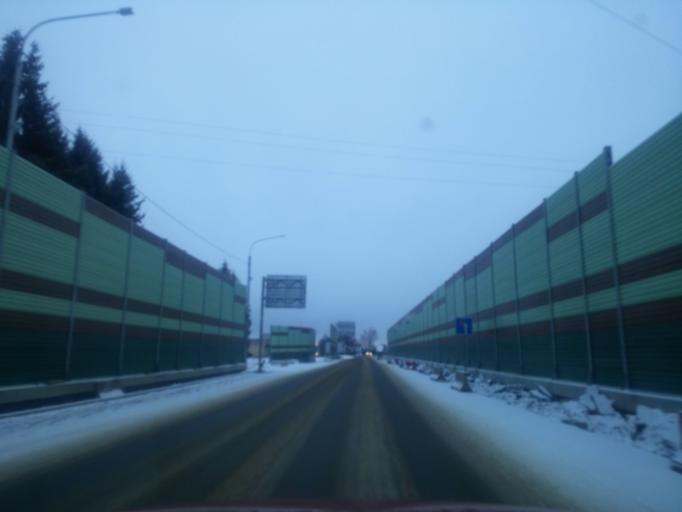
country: RU
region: Tverskaya
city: Likhoslavl'
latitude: 56.9843
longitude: 35.4398
